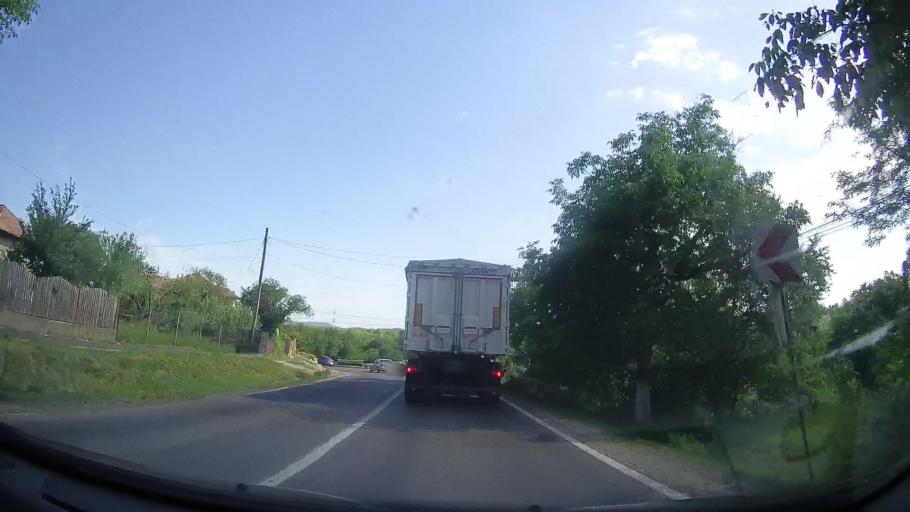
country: RO
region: Prahova
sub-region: Comuna Izvoarele
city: Homoraciu
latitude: 45.2511
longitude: 26.0247
